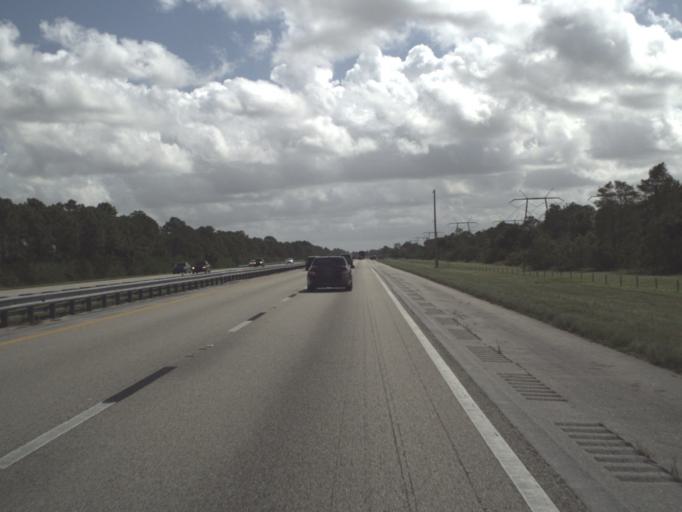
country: US
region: Florida
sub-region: Indian River County
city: West Vero Corridor
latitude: 27.5436
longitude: -80.6240
